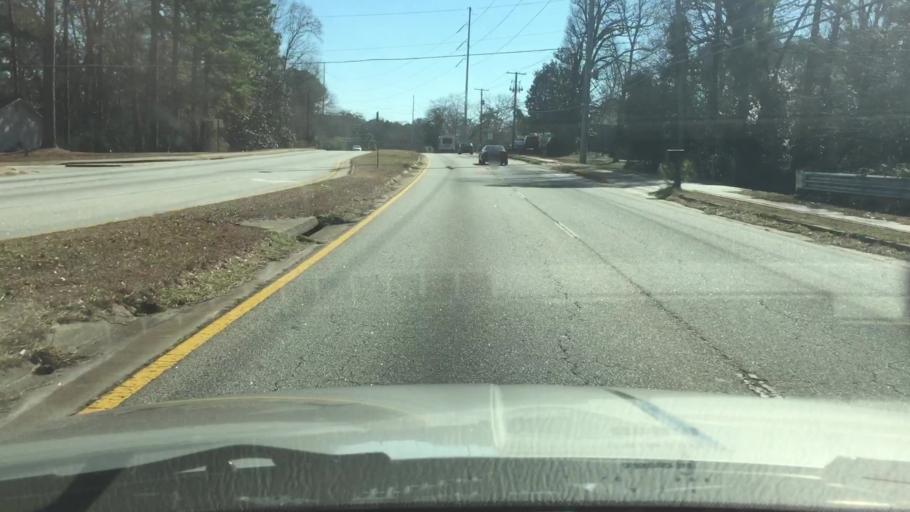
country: US
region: Georgia
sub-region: DeKalb County
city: Redan
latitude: 33.7475
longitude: -84.1970
